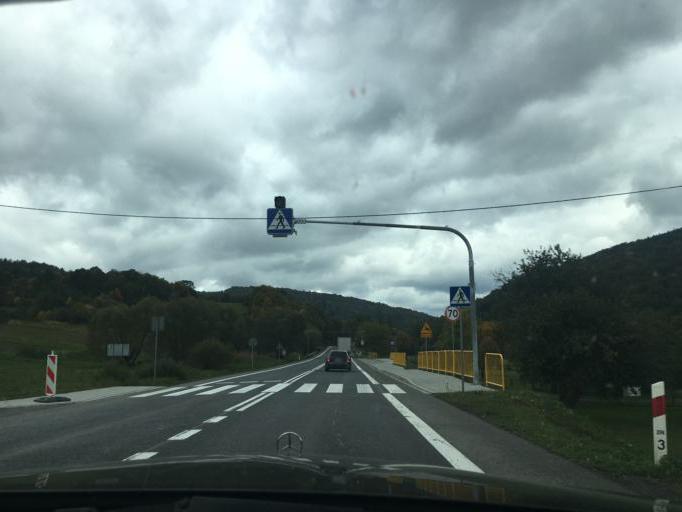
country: PL
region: Subcarpathian Voivodeship
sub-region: Powiat krosnienski
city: Dukla
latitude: 49.5123
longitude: 21.6951
